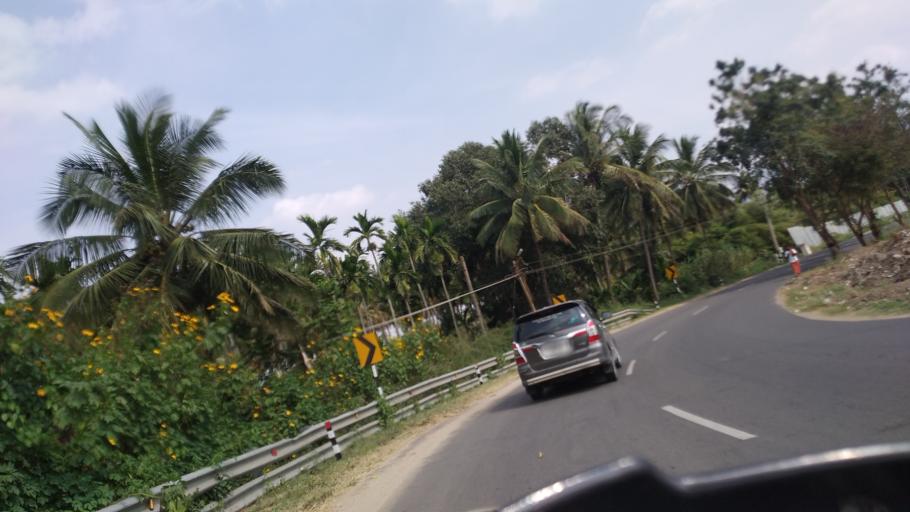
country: IN
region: Tamil Nadu
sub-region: Coimbatore
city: Perur
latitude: 10.9500
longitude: 76.7685
